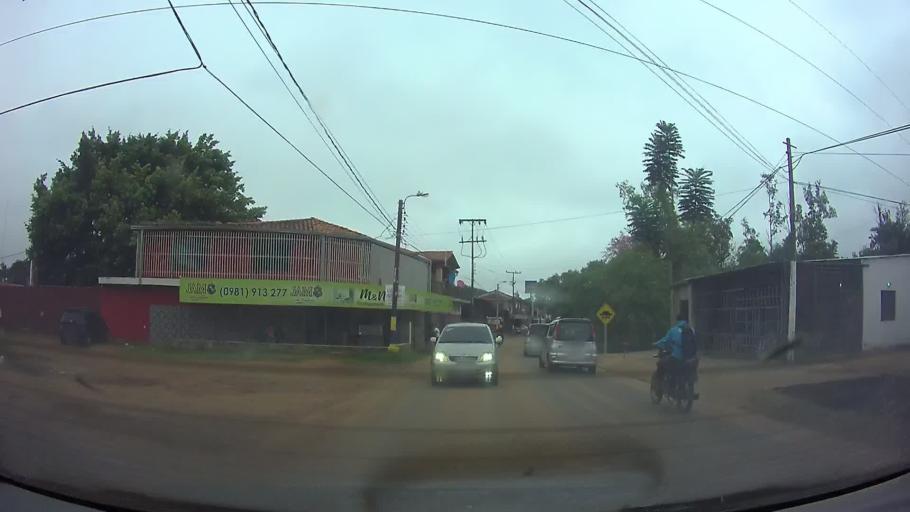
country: PY
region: Central
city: San Lorenzo
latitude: -25.3131
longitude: -57.4927
